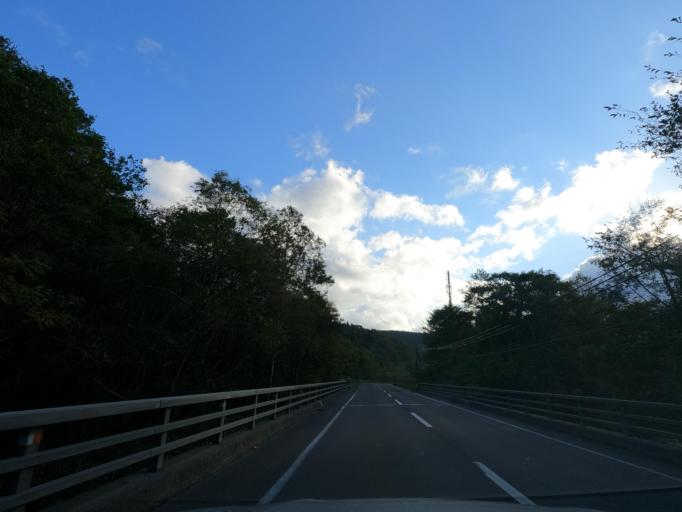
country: JP
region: Hokkaido
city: Shiraoi
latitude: 42.7029
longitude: 141.1390
